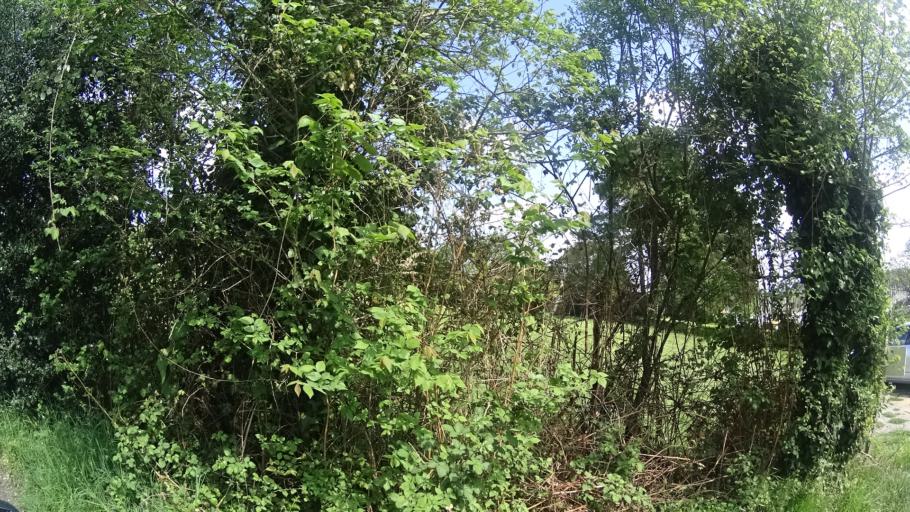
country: FR
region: Brittany
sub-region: Departement du Morbihan
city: Nivillac
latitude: 47.5770
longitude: -2.2838
